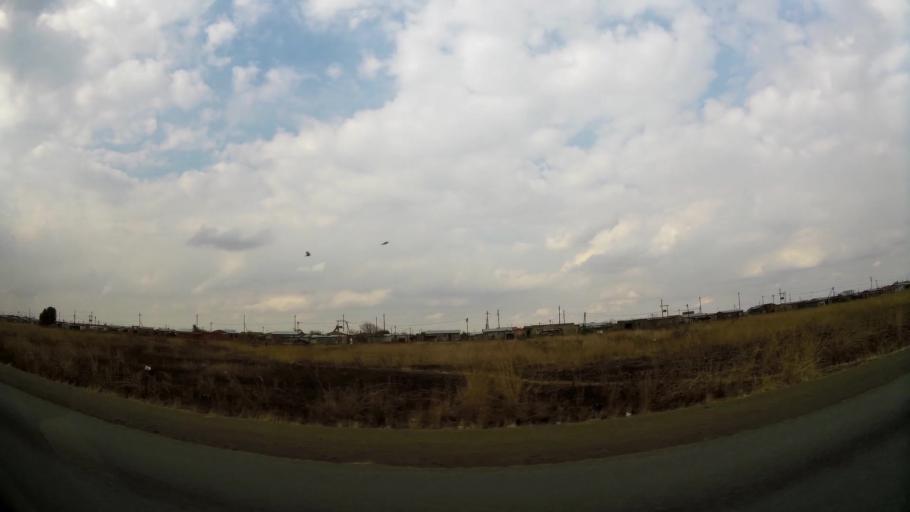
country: ZA
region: Orange Free State
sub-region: Fezile Dabi District Municipality
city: Sasolburg
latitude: -26.8616
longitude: 27.8881
